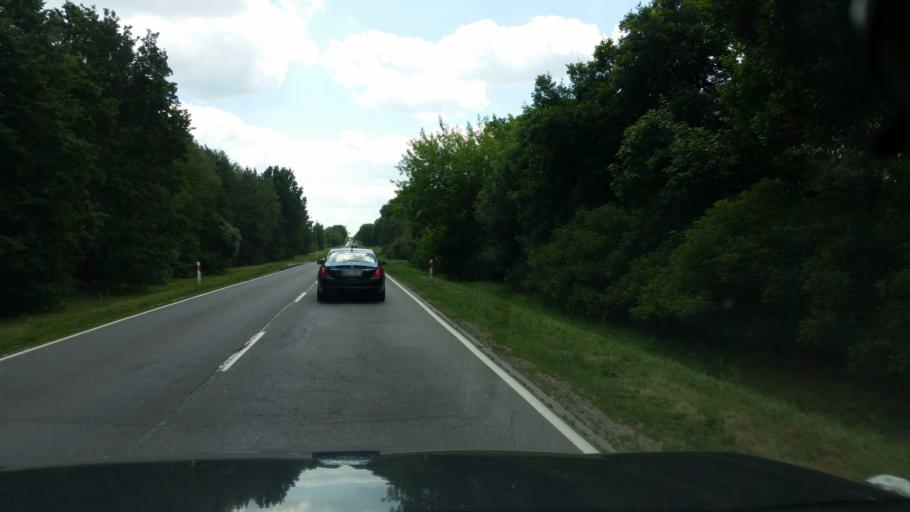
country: PL
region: Masovian Voivodeship
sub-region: Powiat ostrowski
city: Ostrow Mazowiecka
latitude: 52.8511
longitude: 21.8681
